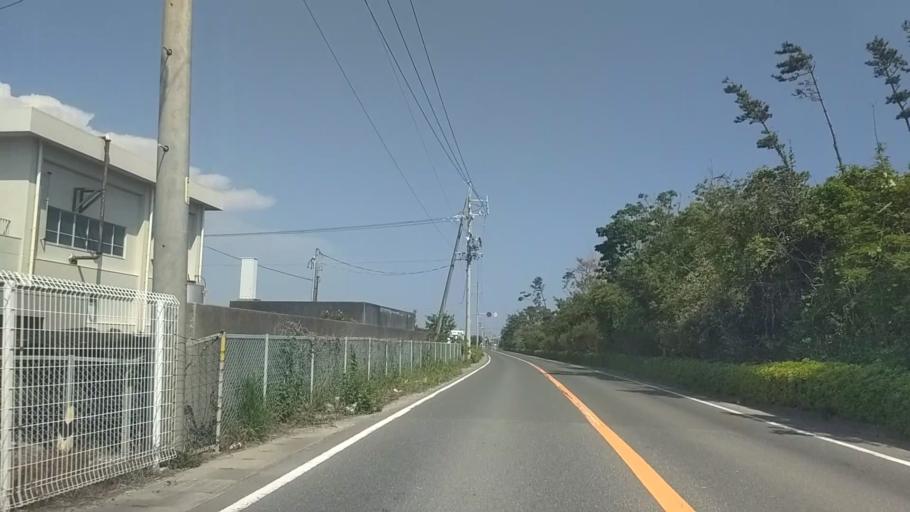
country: JP
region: Shizuoka
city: Hamamatsu
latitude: 34.6689
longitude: 137.7018
